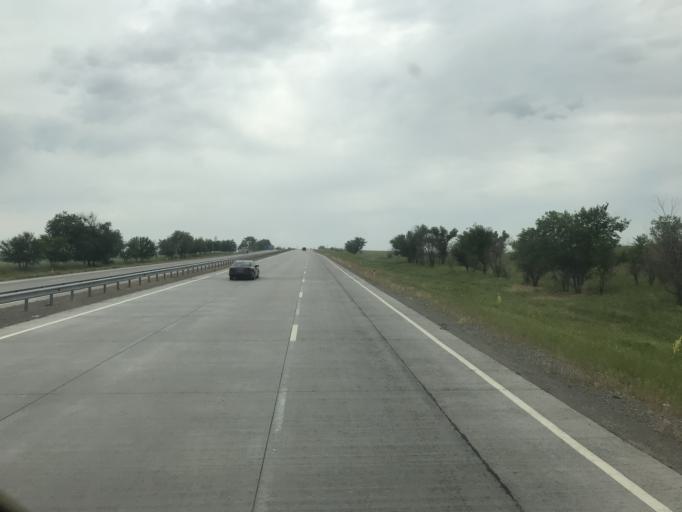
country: KZ
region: Ongtustik Qazaqstan
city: Shymkent
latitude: 42.1943
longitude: 69.5067
